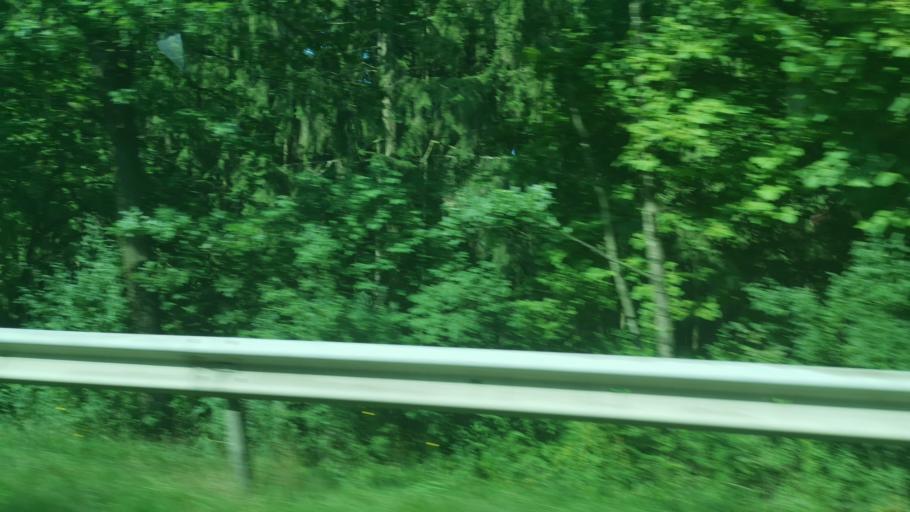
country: DE
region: Bavaria
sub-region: Upper Palatinate
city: Pemfling
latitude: 49.2851
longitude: 12.6257
